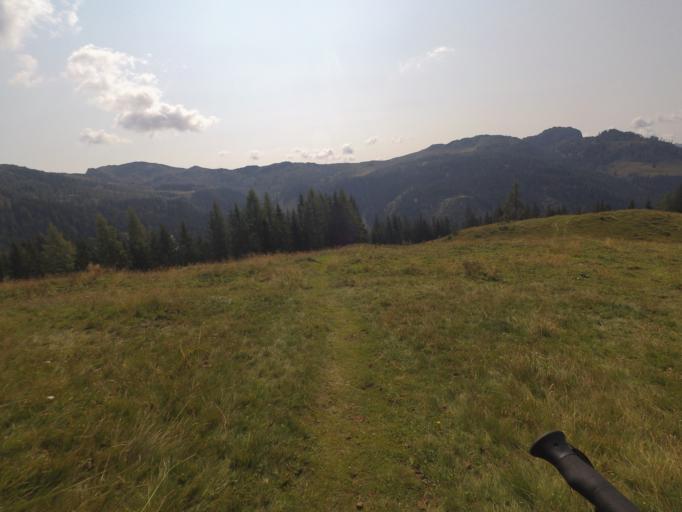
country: AT
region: Salzburg
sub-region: Politischer Bezirk Sankt Johann im Pongau
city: Kleinarl
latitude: 47.2764
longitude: 13.2608
